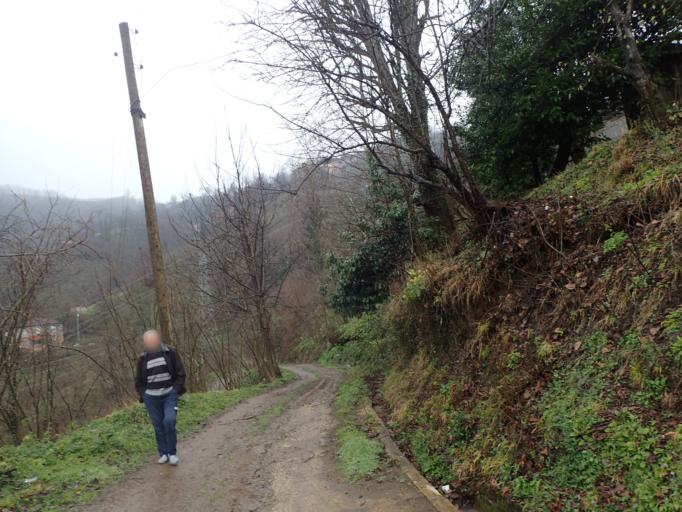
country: TR
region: Ordu
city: Camas
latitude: 40.9121
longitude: 37.5711
